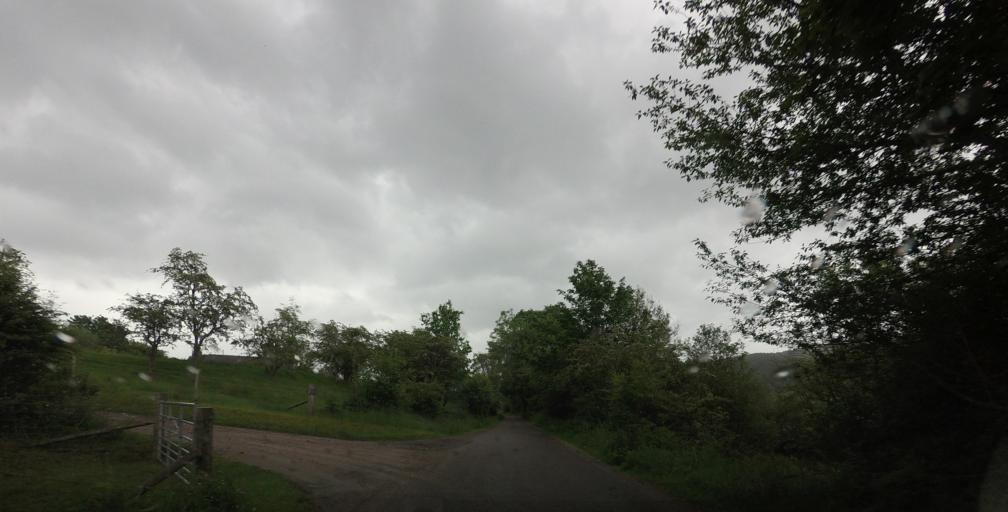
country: GB
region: Scotland
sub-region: Argyll and Bute
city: Oban
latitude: 56.7061
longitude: -5.5675
